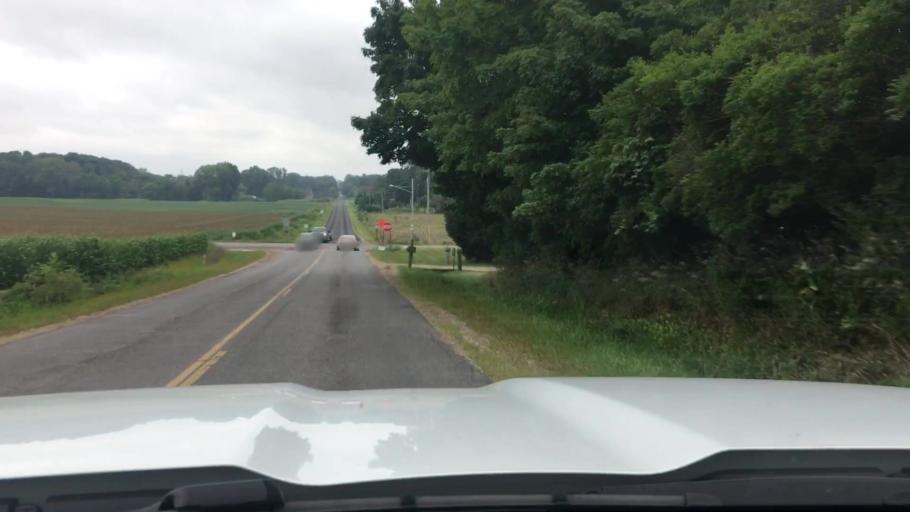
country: US
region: Michigan
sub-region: Ottawa County
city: Hudsonville
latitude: 42.7830
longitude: -85.8616
